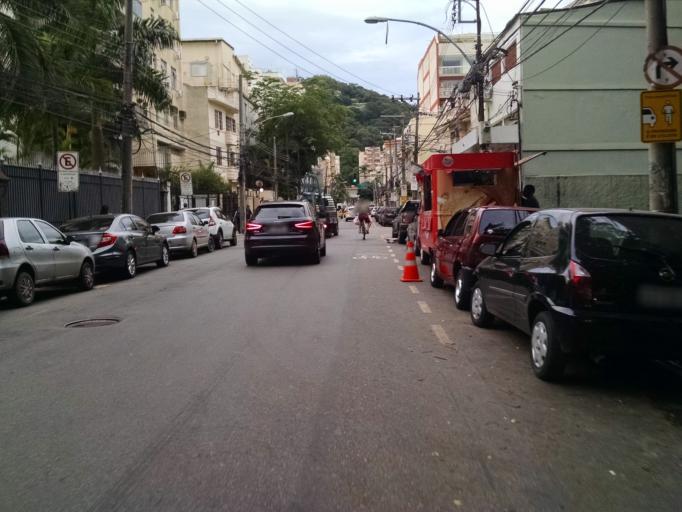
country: BR
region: Rio de Janeiro
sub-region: Rio De Janeiro
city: Rio de Janeiro
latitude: -22.9473
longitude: -43.1858
